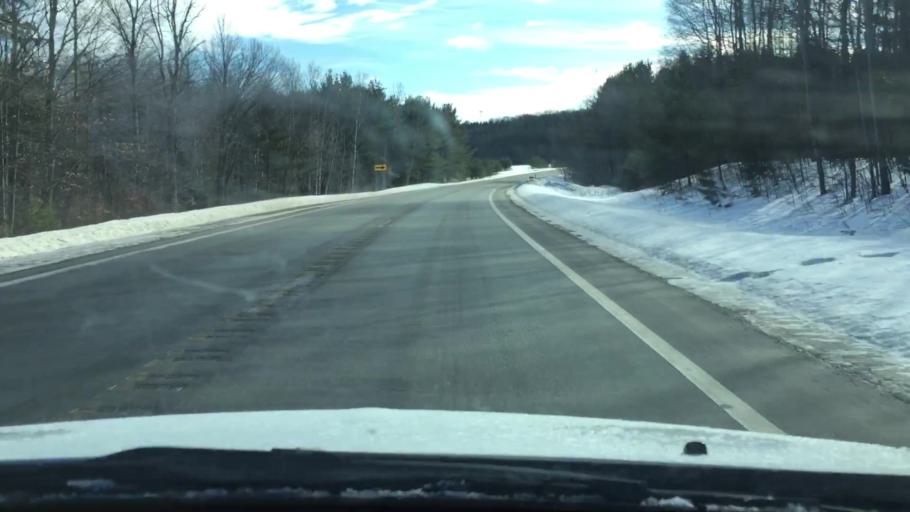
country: US
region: Michigan
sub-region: Antrim County
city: Mancelona
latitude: 44.9833
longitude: -85.0541
